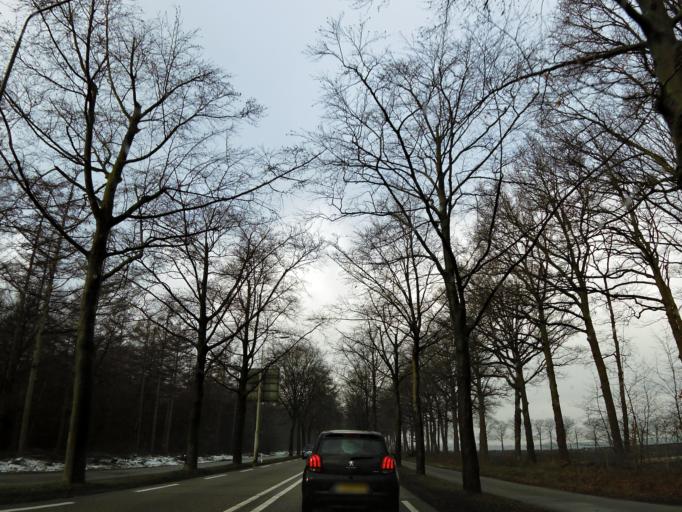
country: NL
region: North Brabant
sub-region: Gemeente Sint Anthonis
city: Sint Anthonis
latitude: 51.5498
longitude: 5.8048
